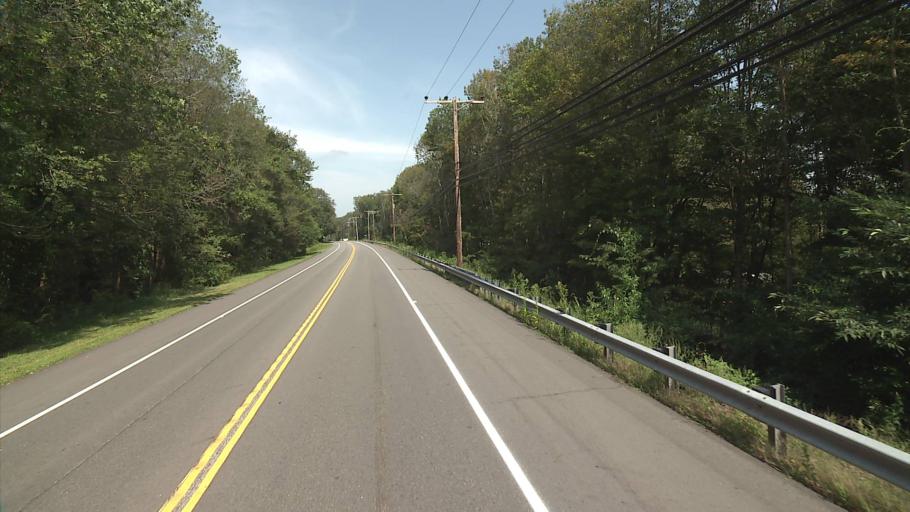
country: US
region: Connecticut
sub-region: New Haven County
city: Madison Center
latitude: 41.3493
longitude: -72.6323
